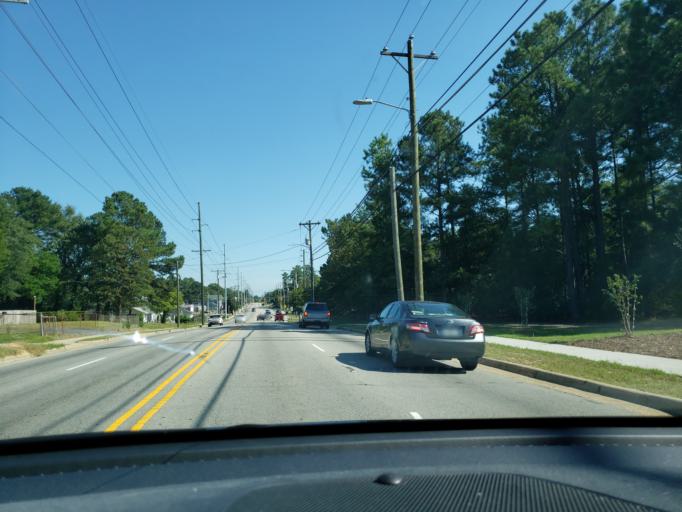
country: US
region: North Carolina
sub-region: Cumberland County
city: Fayetteville
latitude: 35.0866
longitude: -78.9066
